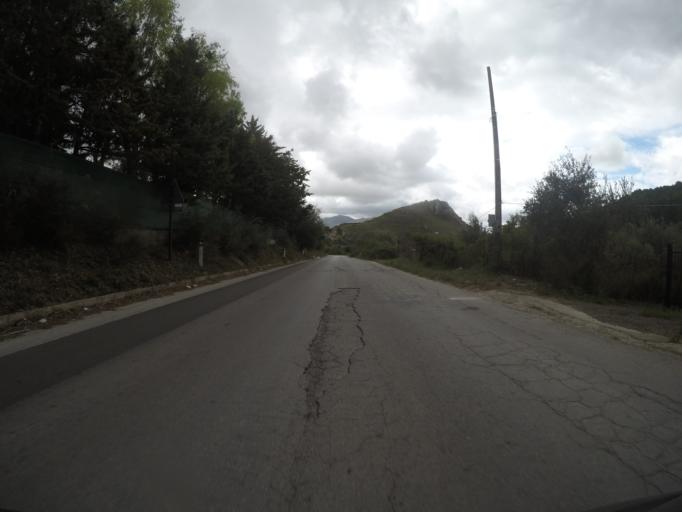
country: IT
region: Sicily
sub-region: Palermo
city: Montelepre
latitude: 38.1034
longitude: 13.1712
